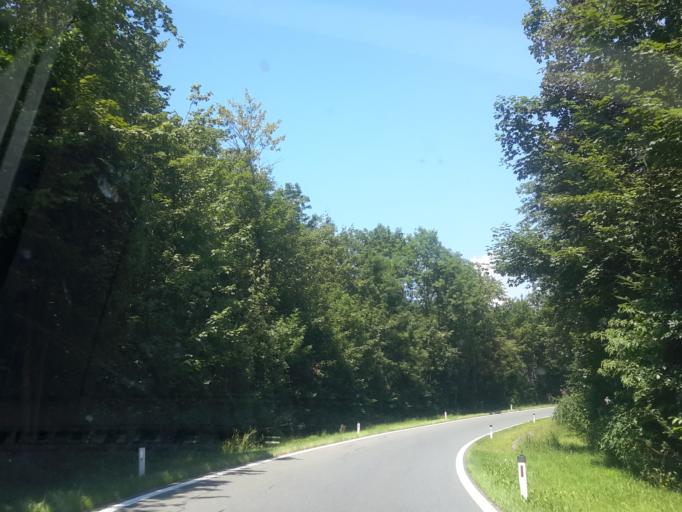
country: AT
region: Tyrol
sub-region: Politischer Bezirk Kufstein
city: Kufstein
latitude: 47.5961
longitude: 12.1767
